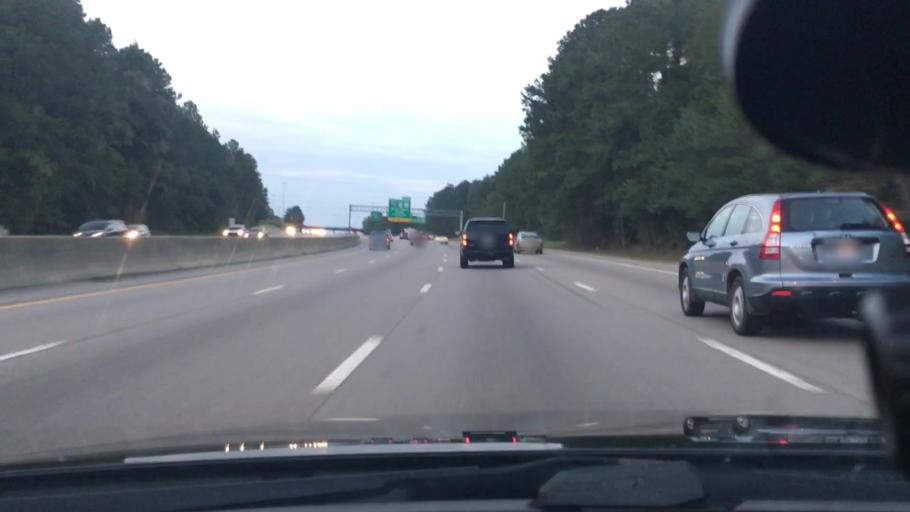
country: US
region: North Carolina
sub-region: Wake County
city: Garner
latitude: 35.7616
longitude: -78.5746
